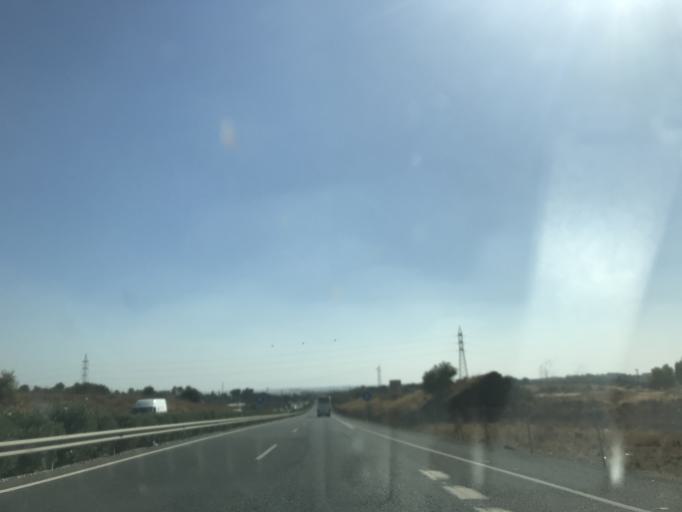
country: ES
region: Andalusia
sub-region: Provincia de Sevilla
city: Alcala de Guadaira
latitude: 37.3392
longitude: -5.8210
